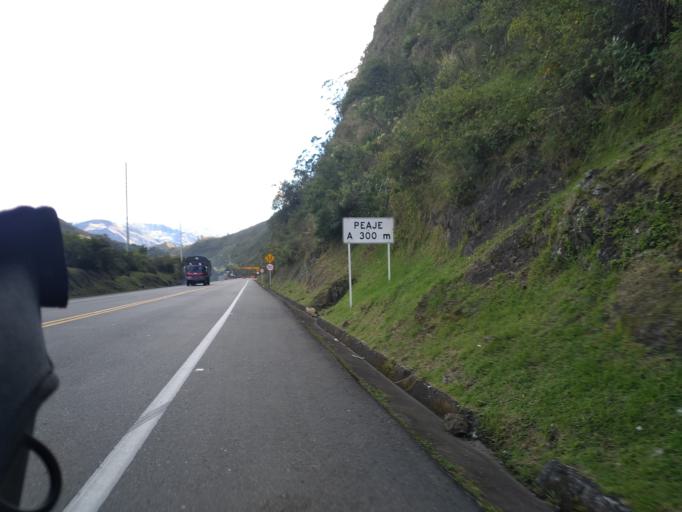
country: CO
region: Narino
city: Tangua
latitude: 1.0882
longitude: -77.4059
